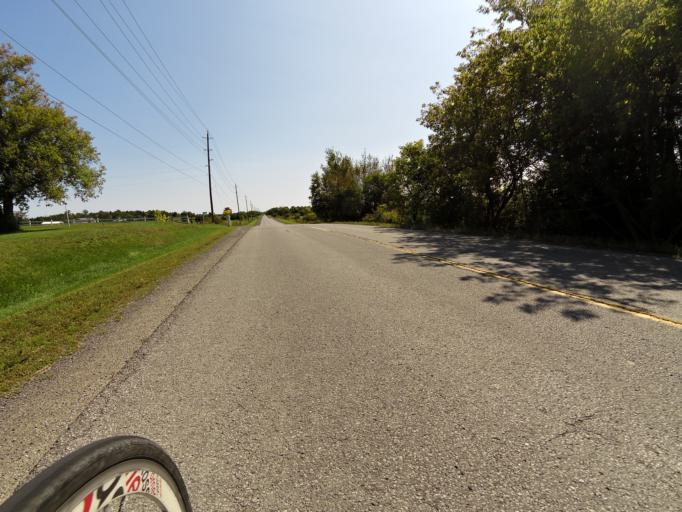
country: CA
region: Ontario
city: Arnprior
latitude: 45.4701
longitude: -76.1094
